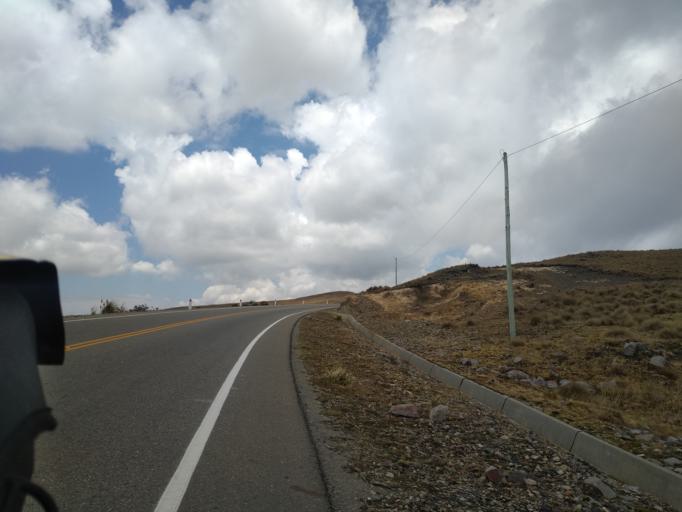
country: PE
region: La Libertad
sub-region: Provincia de Santiago de Chuco
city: Quiruvilca
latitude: -7.9525
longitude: -78.1914
